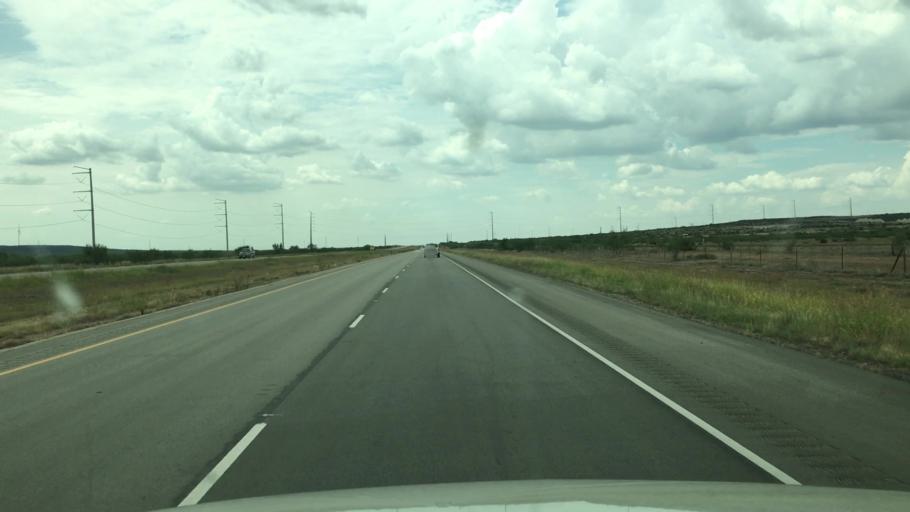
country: US
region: Texas
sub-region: Glasscock County
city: Garden City
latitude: 31.9813
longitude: -101.2557
